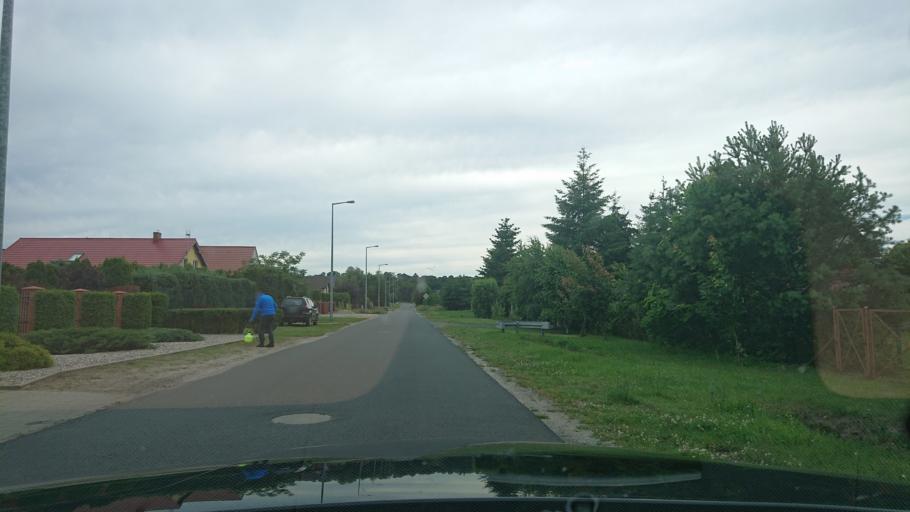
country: PL
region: Greater Poland Voivodeship
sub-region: Powiat gnieznienski
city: Gniezno
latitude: 52.5101
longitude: 17.6142
